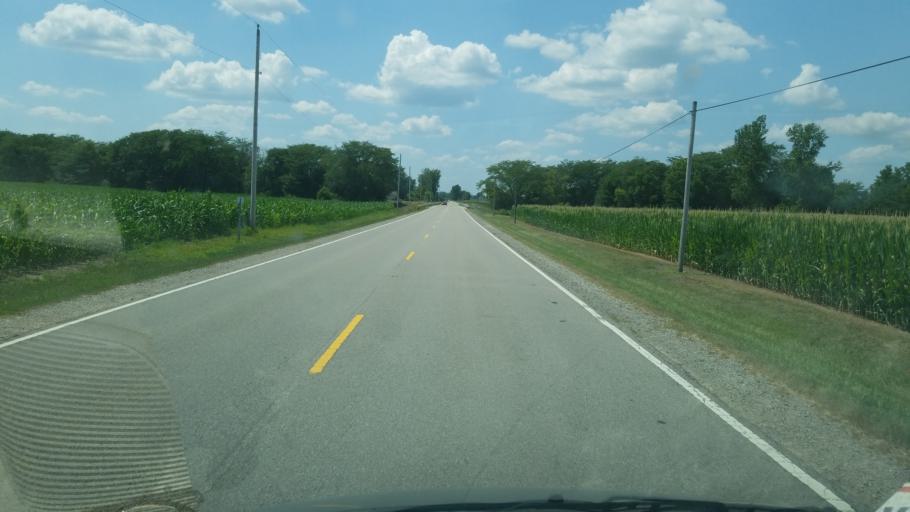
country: US
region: Ohio
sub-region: Champaign County
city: North Lewisburg
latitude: 40.1495
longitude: -83.4819
